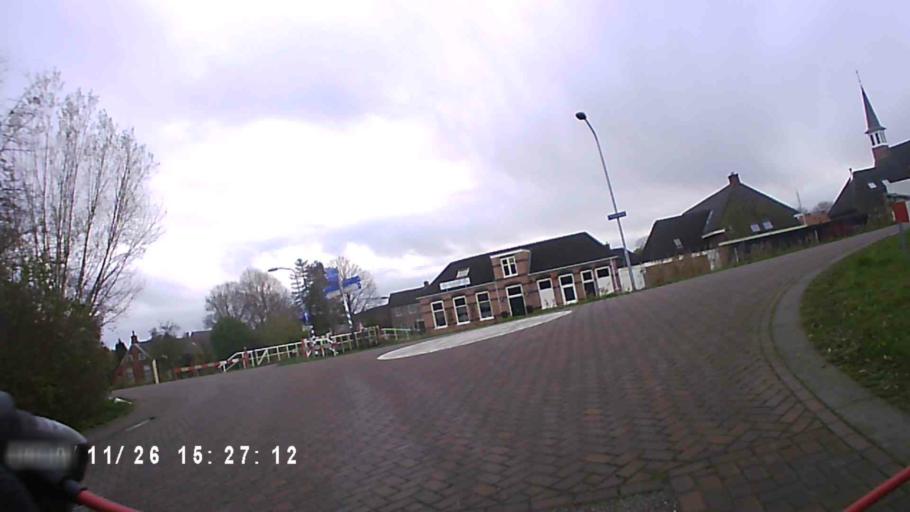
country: NL
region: Groningen
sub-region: Gemeente Appingedam
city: Appingedam
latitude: 53.3120
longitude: 6.7699
